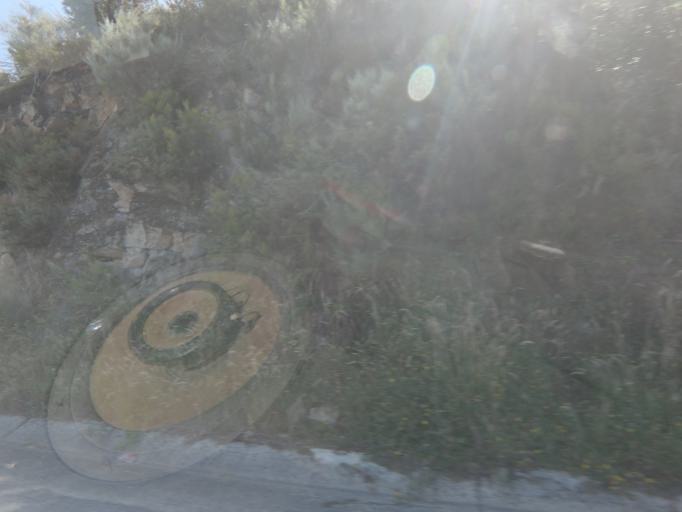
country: PT
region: Viseu
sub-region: Tarouca
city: Tarouca
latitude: 40.9975
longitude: -7.7811
